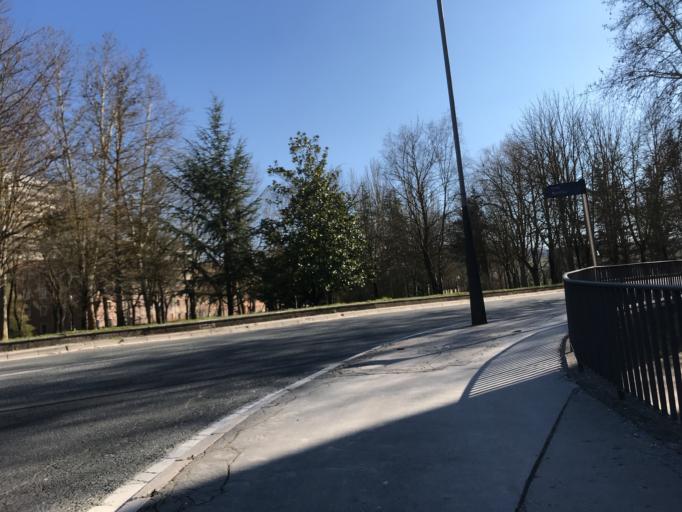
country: ES
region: Basque Country
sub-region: Provincia de Alava
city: Gasteiz / Vitoria
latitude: 42.8352
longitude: -2.6608
